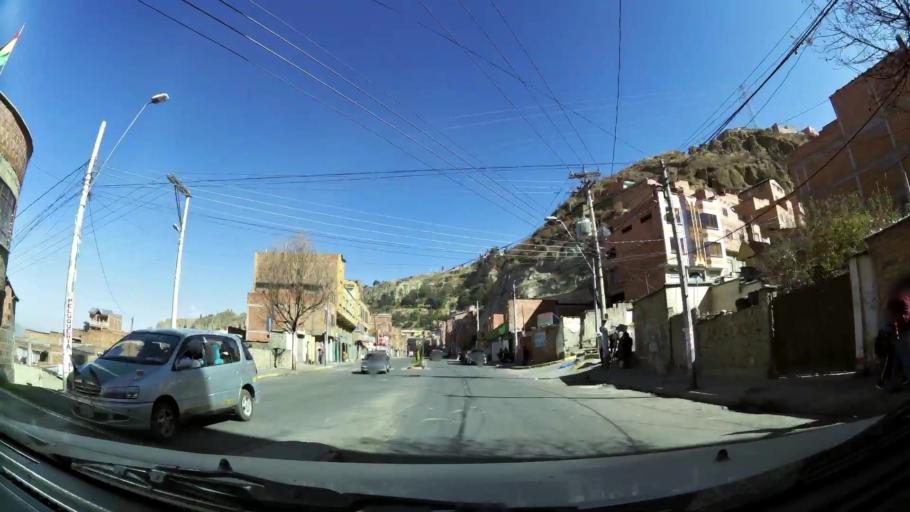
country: BO
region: La Paz
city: La Paz
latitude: -16.5116
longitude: -68.1439
